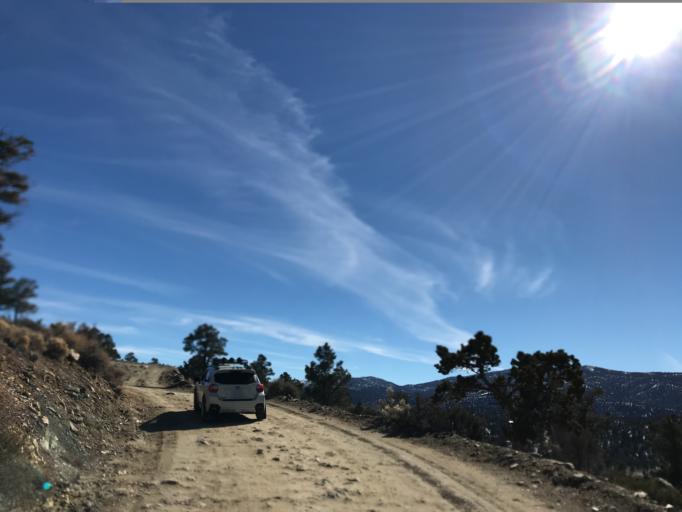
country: US
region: California
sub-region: San Bernardino County
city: Big Bear City
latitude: 34.2731
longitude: -116.7858
